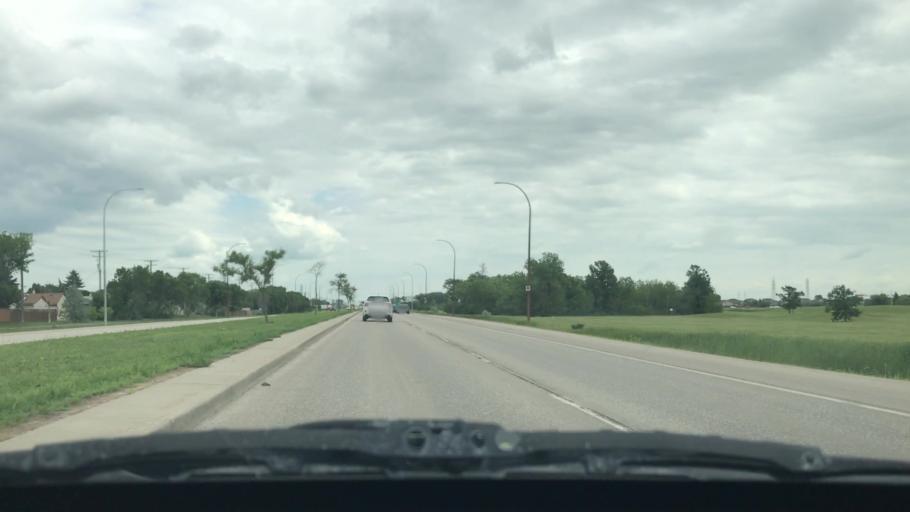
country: CA
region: Manitoba
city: Winnipeg
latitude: 49.8559
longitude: -97.0595
